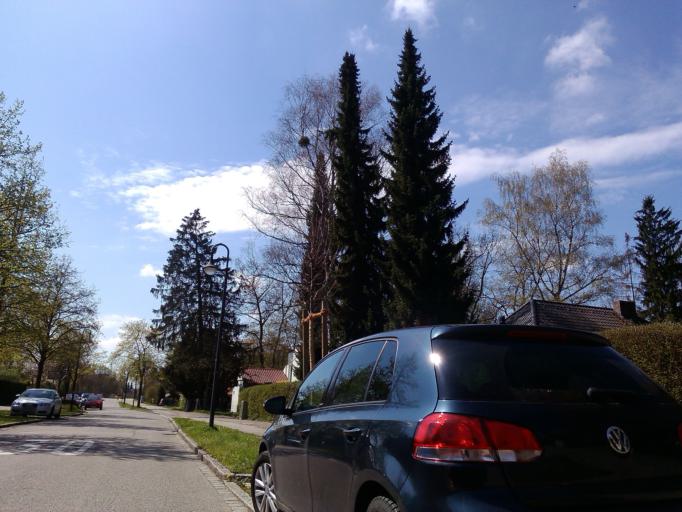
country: DE
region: Bavaria
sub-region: Upper Bavaria
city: Grafelfing
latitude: 48.1294
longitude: 11.4398
